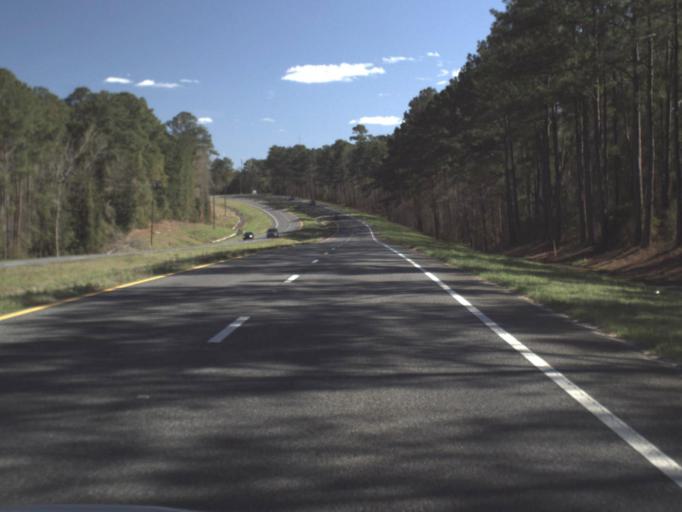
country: US
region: Florida
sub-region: Gadsden County
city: Midway
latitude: 30.5219
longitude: -84.4686
